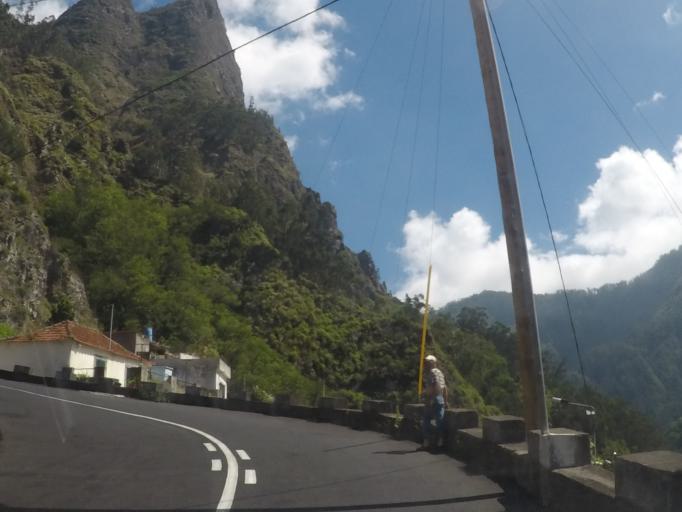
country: PT
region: Madeira
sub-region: Camara de Lobos
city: Curral das Freiras
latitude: 32.7157
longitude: -16.9674
